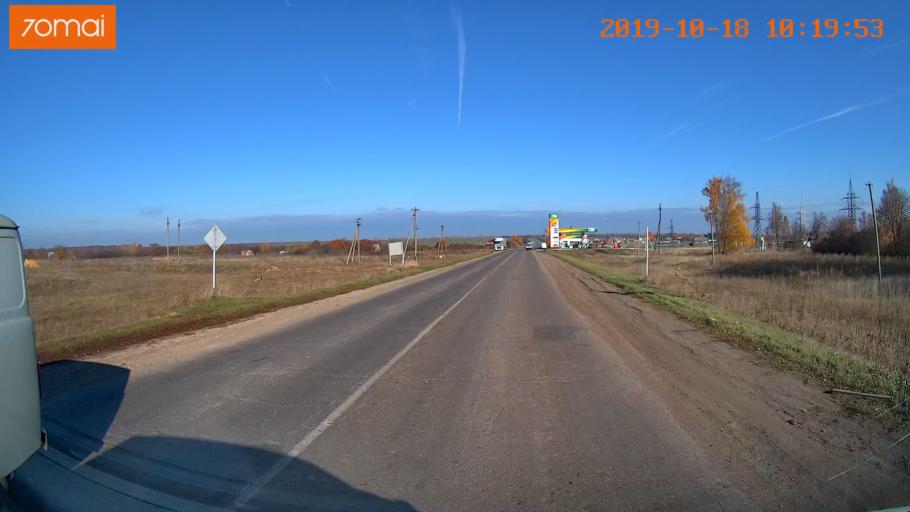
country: RU
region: Tula
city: Kurkino
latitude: 53.4249
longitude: 38.6448
